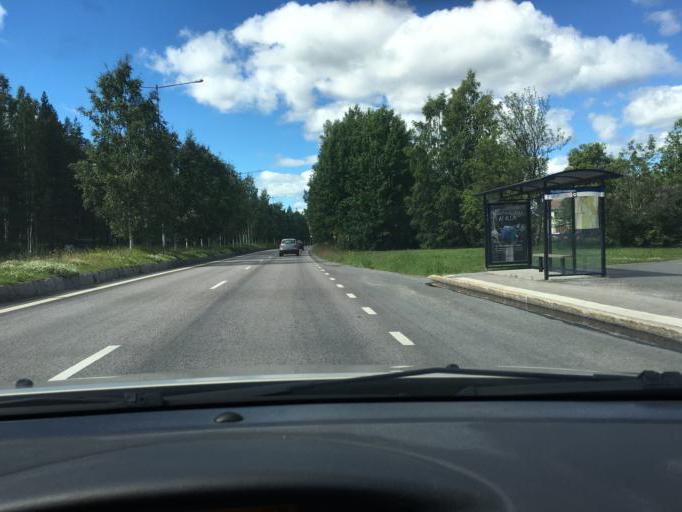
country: SE
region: Norrbotten
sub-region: Lulea Kommun
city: Bergnaset
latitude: 65.5773
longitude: 22.1036
